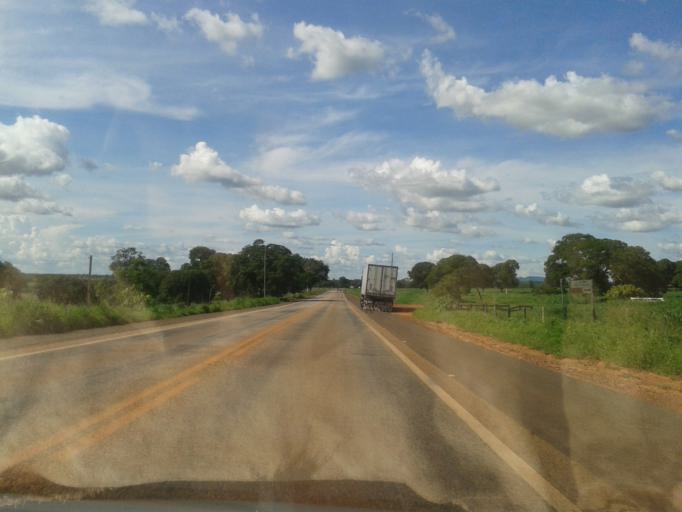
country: BR
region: Goias
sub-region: Mozarlandia
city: Mozarlandia
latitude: -15.0905
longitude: -50.6219
